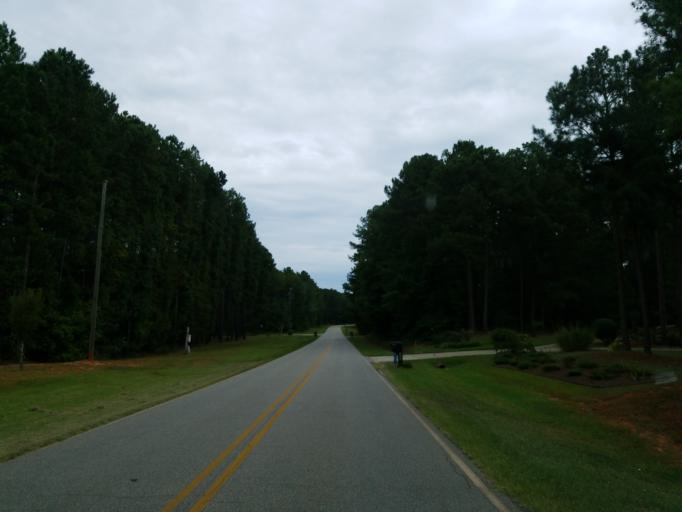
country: US
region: Georgia
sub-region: Monroe County
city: Forsyth
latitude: 32.9413
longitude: -83.9398
